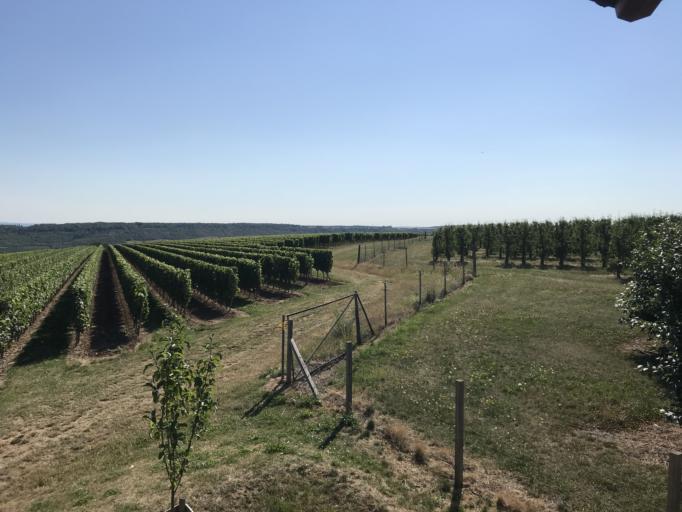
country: DE
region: Rheinland-Pfalz
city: Ockenheim
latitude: 49.9391
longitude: 7.9954
